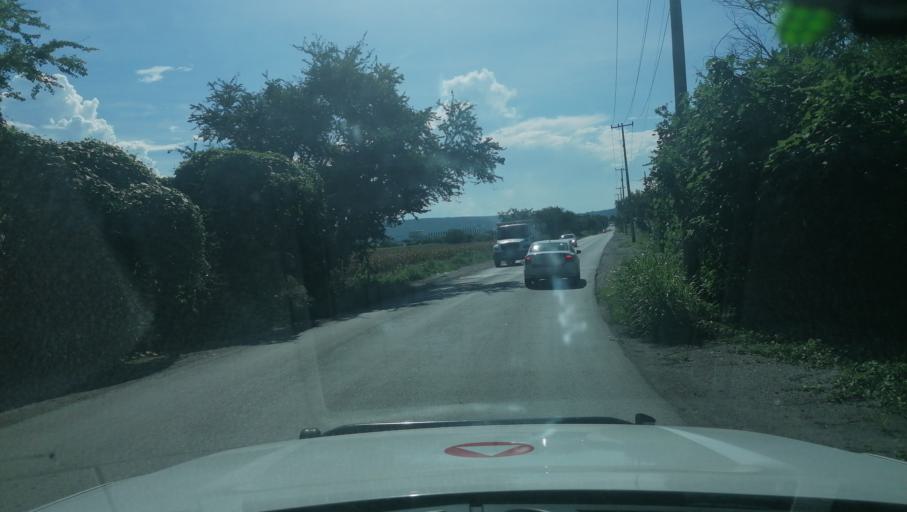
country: MX
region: Morelos
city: Zacatepec
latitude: 18.6586
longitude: -99.1794
